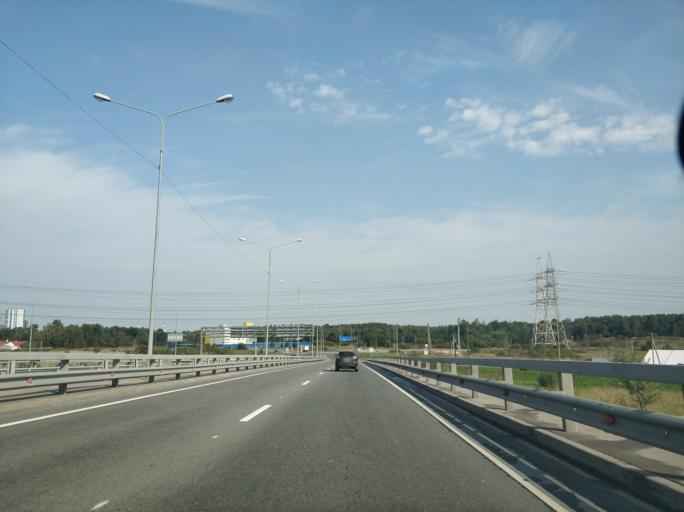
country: RU
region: Leningrad
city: Murino
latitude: 60.0189
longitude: 30.4624
